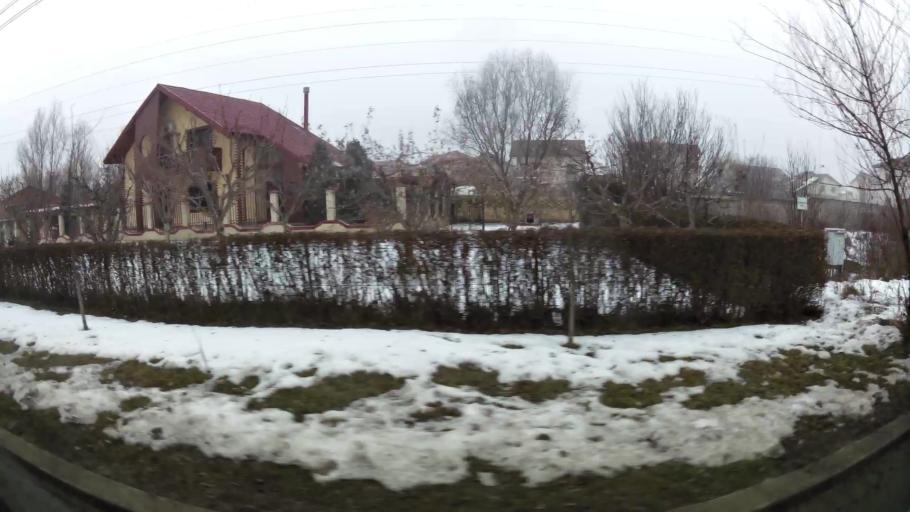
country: RO
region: Ilfov
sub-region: Comuna Chiajna
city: Rosu
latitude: 44.4463
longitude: 26.0011
